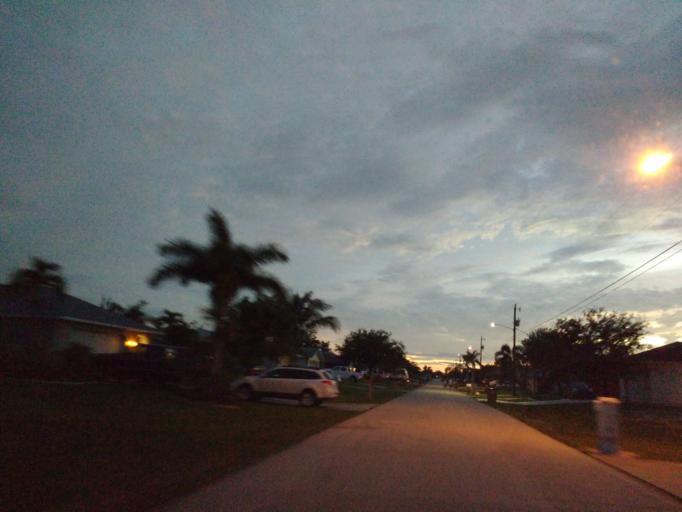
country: US
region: Florida
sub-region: Lee County
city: Cape Coral
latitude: 26.6209
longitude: -81.9686
